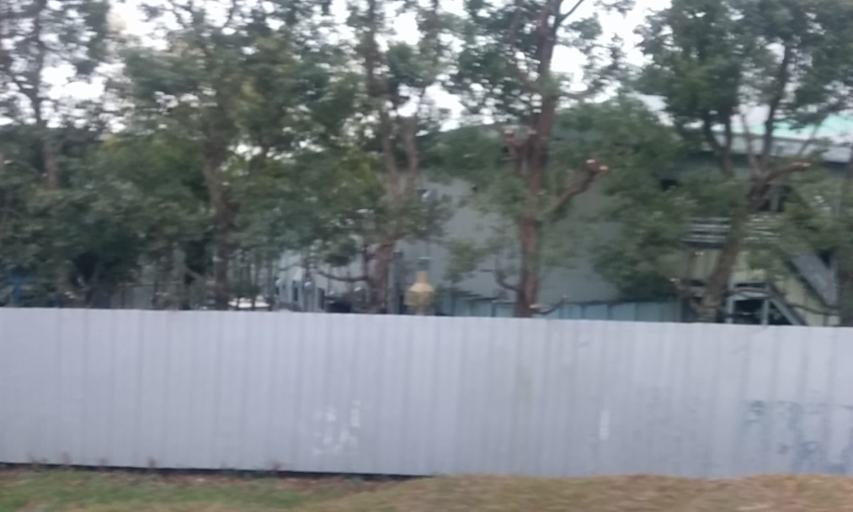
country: JP
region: Tokyo
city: Kokubunji
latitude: 35.6584
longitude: 139.4523
